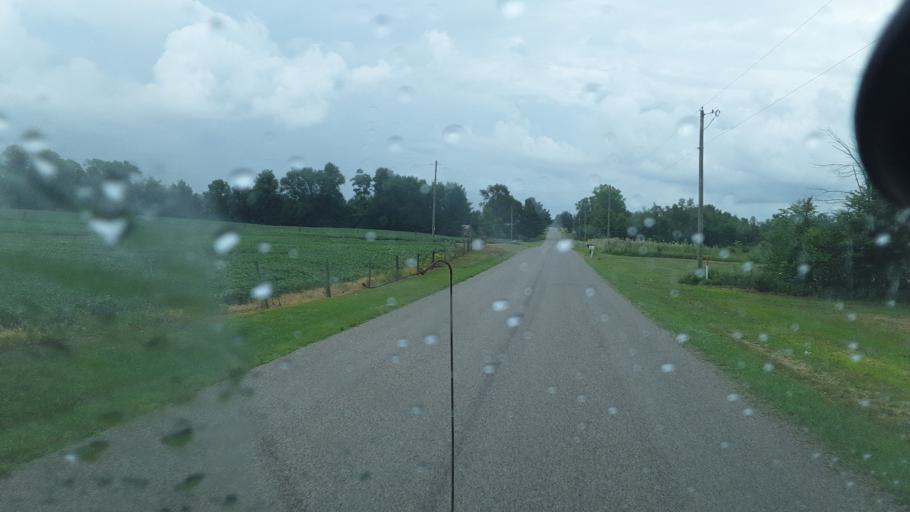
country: US
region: Indiana
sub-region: Steuben County
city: Fremont
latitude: 41.6753
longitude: -84.7961
